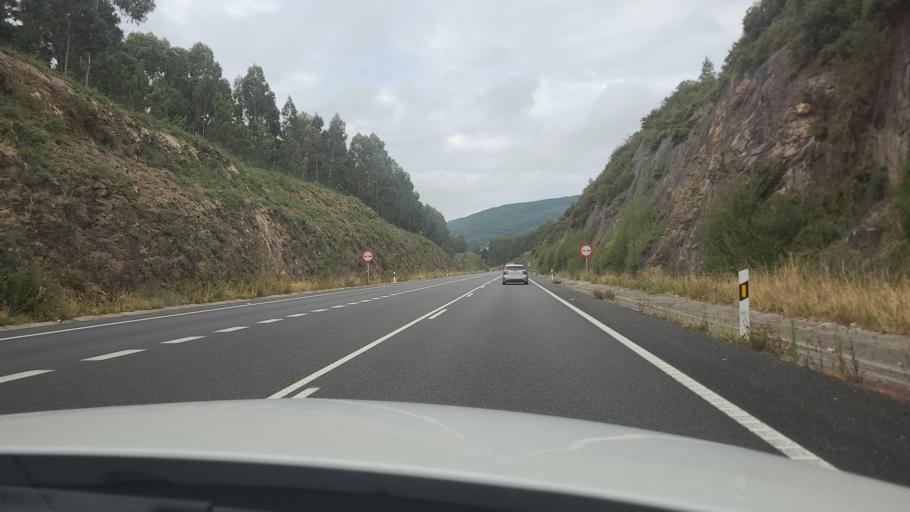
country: ES
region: Galicia
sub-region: Provincia da Coruna
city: Corcubion
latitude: 42.9494
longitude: -9.2187
